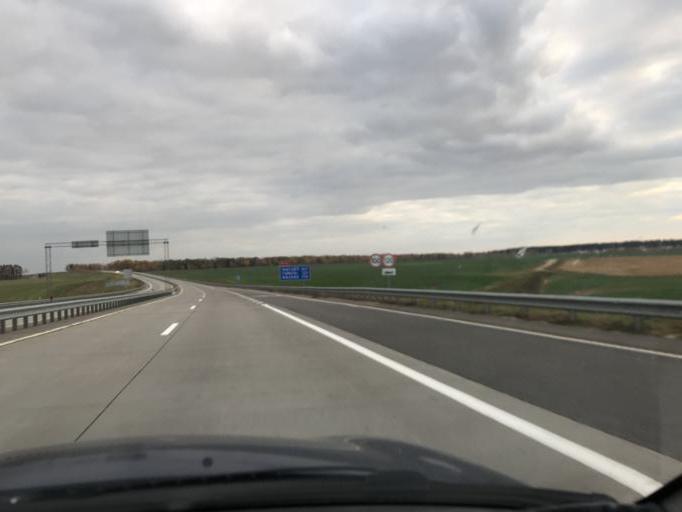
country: BY
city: Fanipol
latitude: 53.7740
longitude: 27.3594
